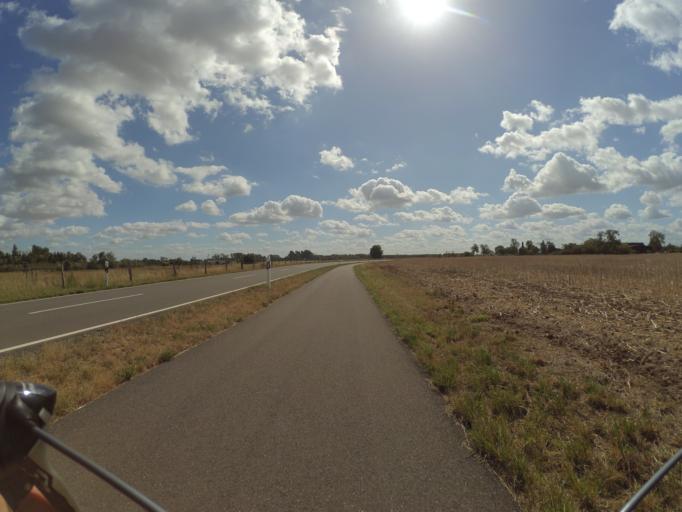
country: DE
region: North Rhine-Westphalia
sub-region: Regierungsbezirk Koln
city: Inden
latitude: 50.8892
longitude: 6.3772
